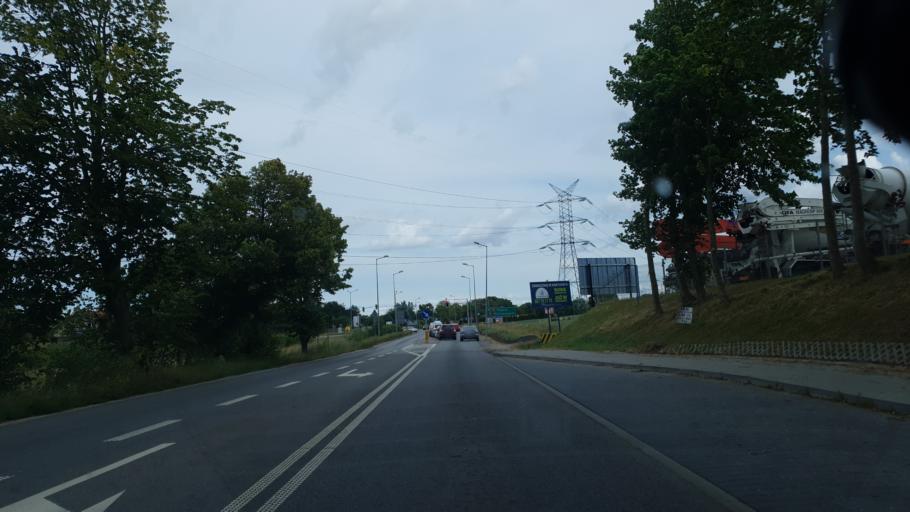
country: PL
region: Pomeranian Voivodeship
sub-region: Powiat kartuski
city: Zukowo
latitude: 54.3807
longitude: 18.3590
